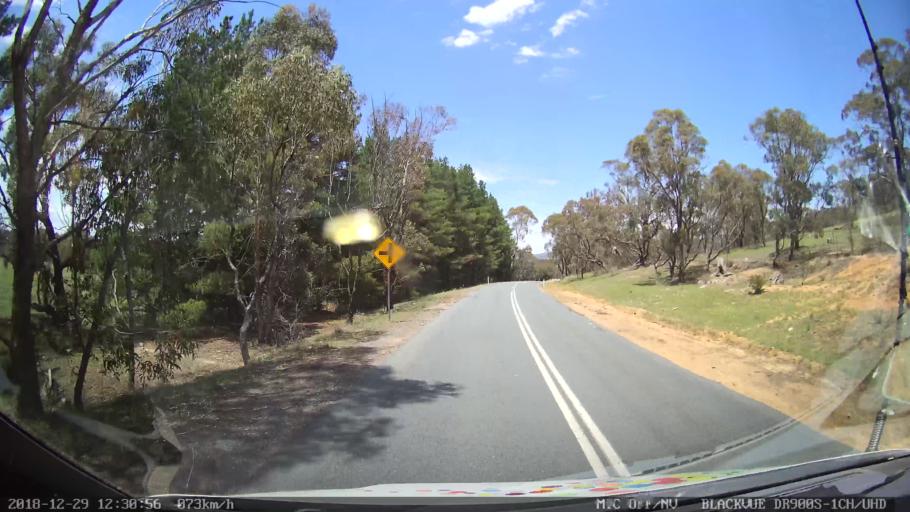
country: AU
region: Australian Capital Territory
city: Macarthur
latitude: -35.5106
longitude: 149.2330
